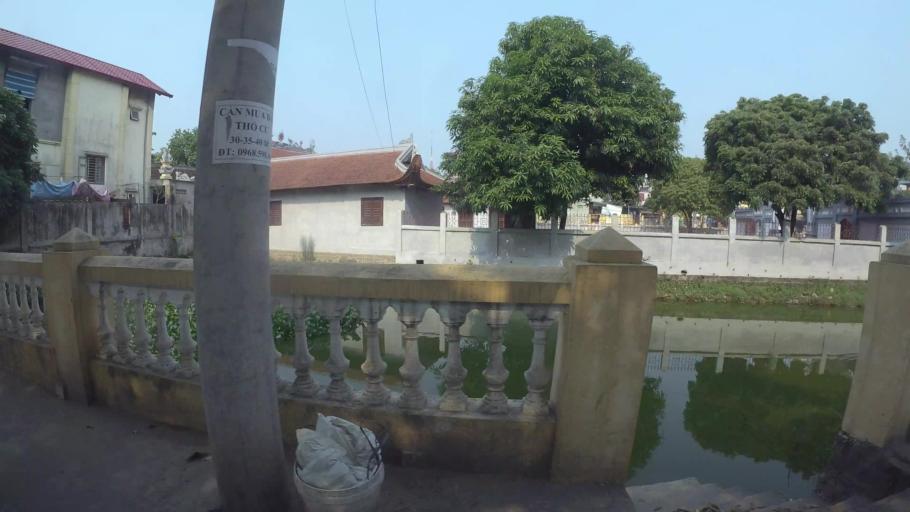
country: VN
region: Ha Noi
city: Ha Dong
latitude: 20.9988
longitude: 105.7530
